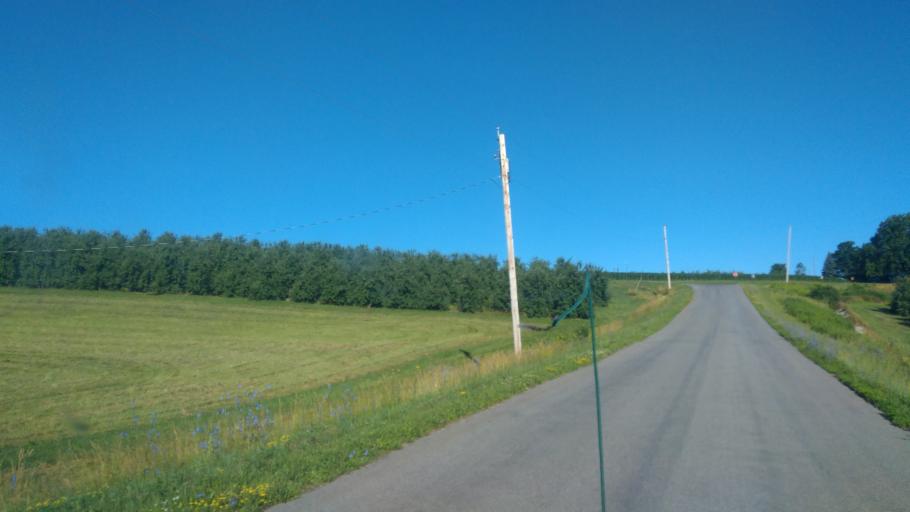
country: US
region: New York
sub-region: Wayne County
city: Sodus
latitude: 43.2005
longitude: -77.0997
